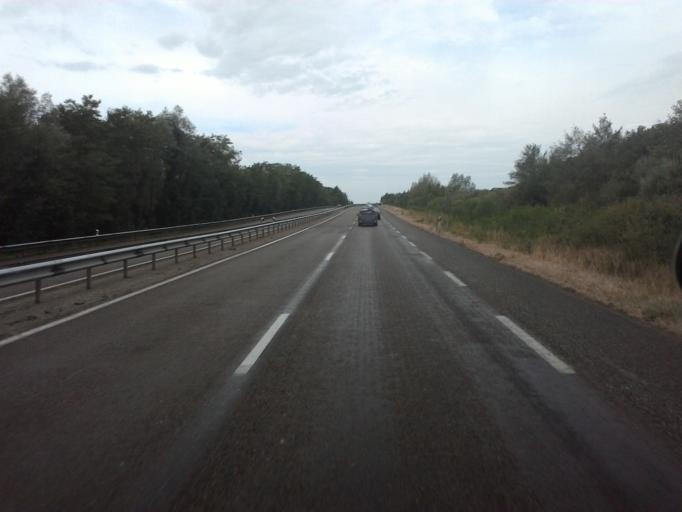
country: FR
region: Franche-Comte
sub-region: Departement du Jura
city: Poligny
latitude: 46.8419
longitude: 5.6644
